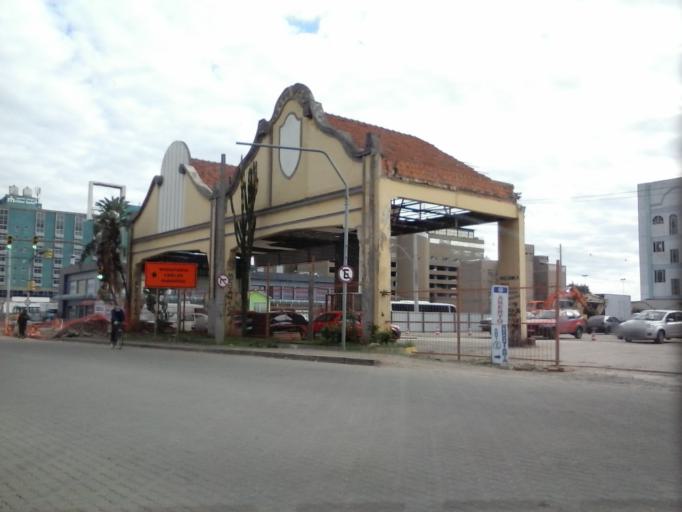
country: BR
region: Rio Grande do Sul
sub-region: Porto Alegre
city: Porto Alegre
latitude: -30.0231
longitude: -51.2160
